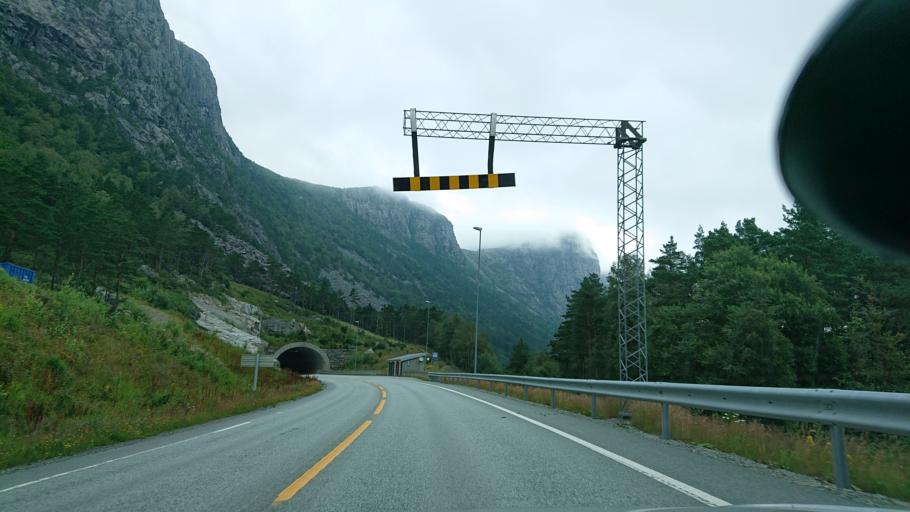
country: NO
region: Rogaland
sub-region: Strand
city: Jorpeland
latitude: 59.0779
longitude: 6.0680
